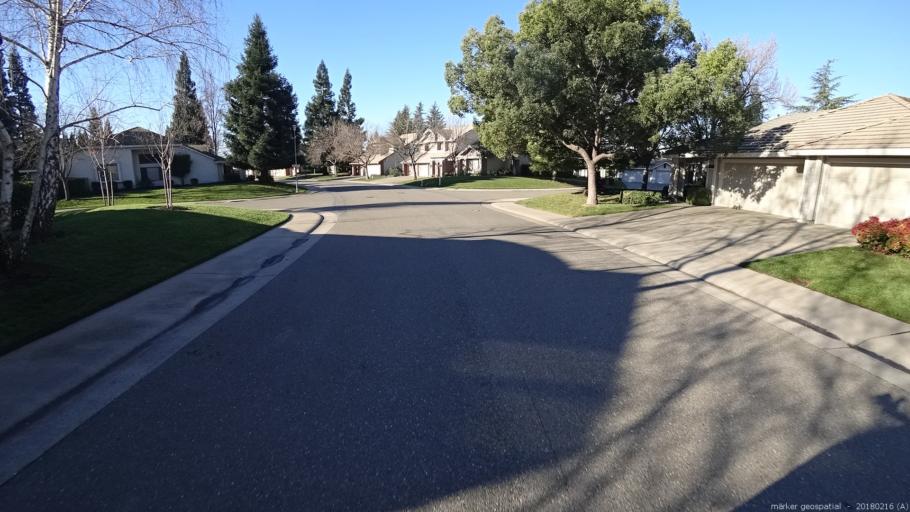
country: US
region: California
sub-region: Sacramento County
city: Gold River
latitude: 38.6289
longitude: -121.2366
